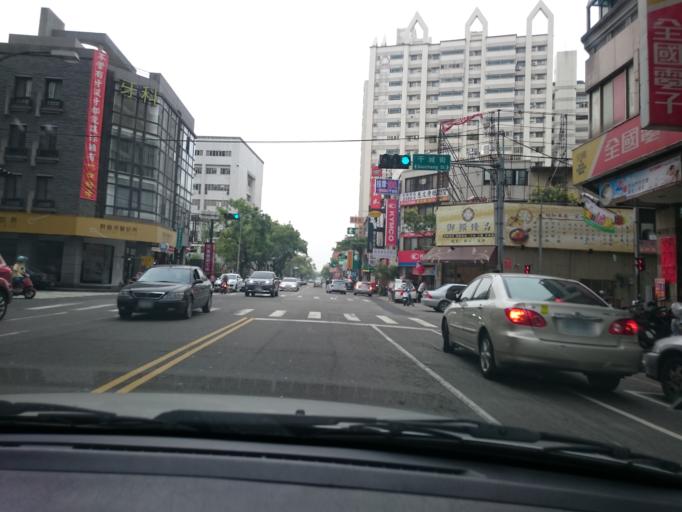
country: TW
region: Taiwan
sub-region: Taichung City
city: Taichung
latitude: 24.1525
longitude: 120.6350
